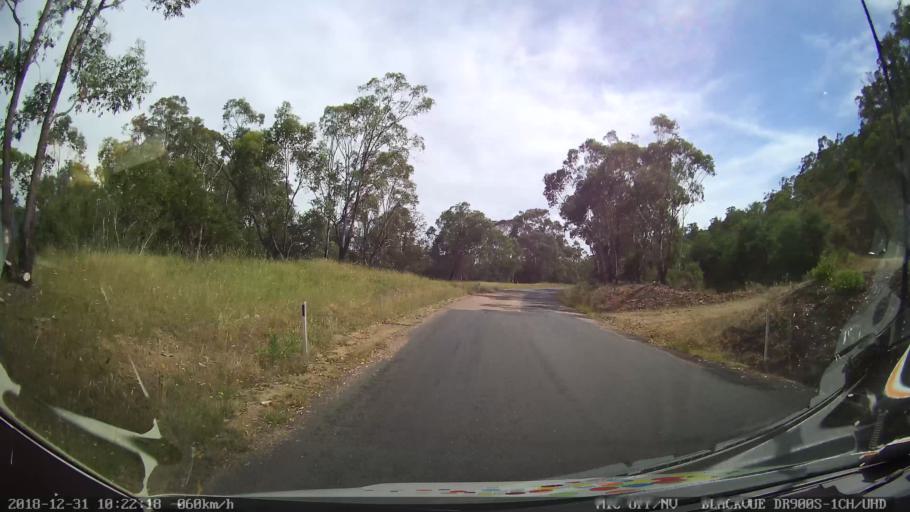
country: AU
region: New South Wales
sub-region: Snowy River
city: Jindabyne
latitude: -36.5268
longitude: 148.1428
